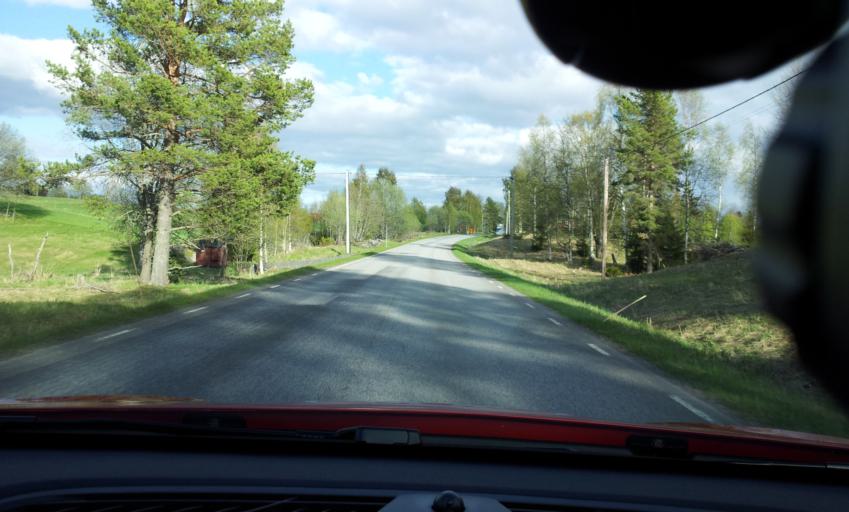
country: SE
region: Jaemtland
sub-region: Krokoms Kommun
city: Krokom
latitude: 63.2674
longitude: 14.3879
